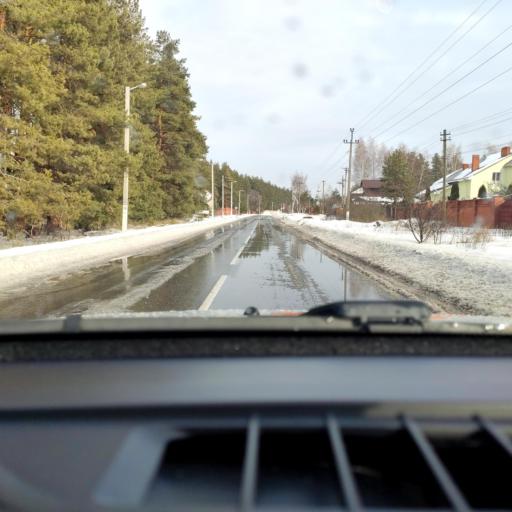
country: RU
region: Voronezj
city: Podgornoye
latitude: 51.7819
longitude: 39.1375
